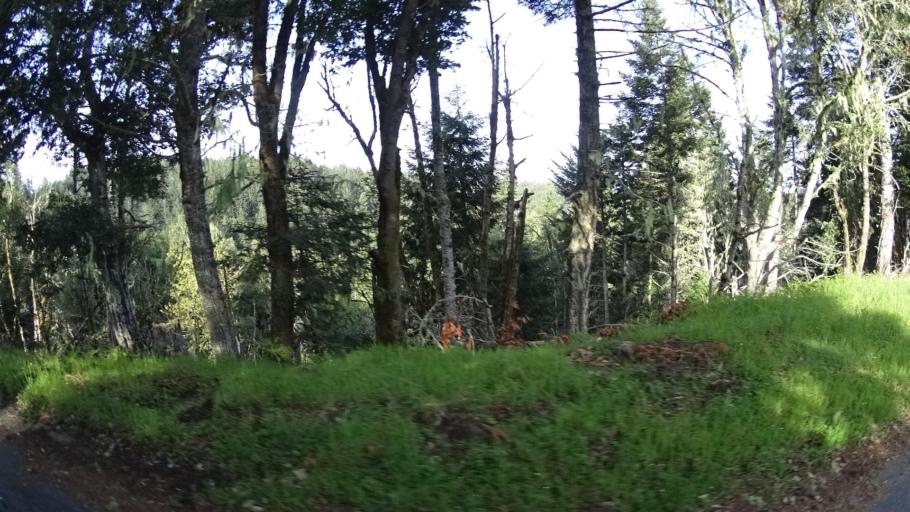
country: US
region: California
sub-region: Humboldt County
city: Hydesville
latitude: 40.6507
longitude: -123.9243
